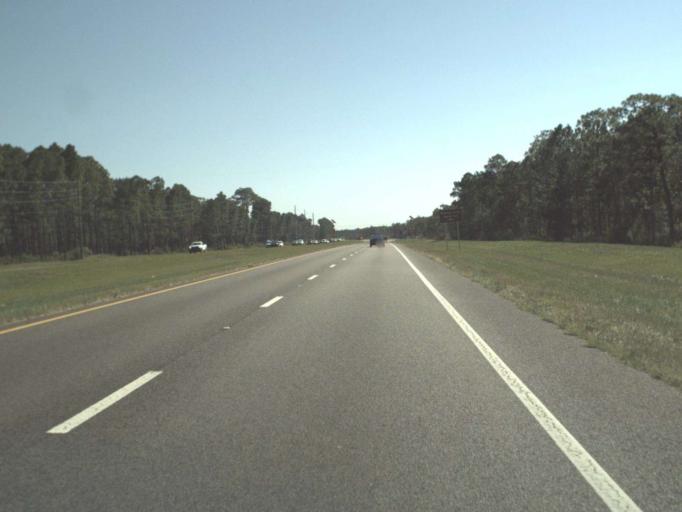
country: US
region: Florida
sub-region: Walton County
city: Seaside
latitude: 30.3608
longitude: -86.1621
